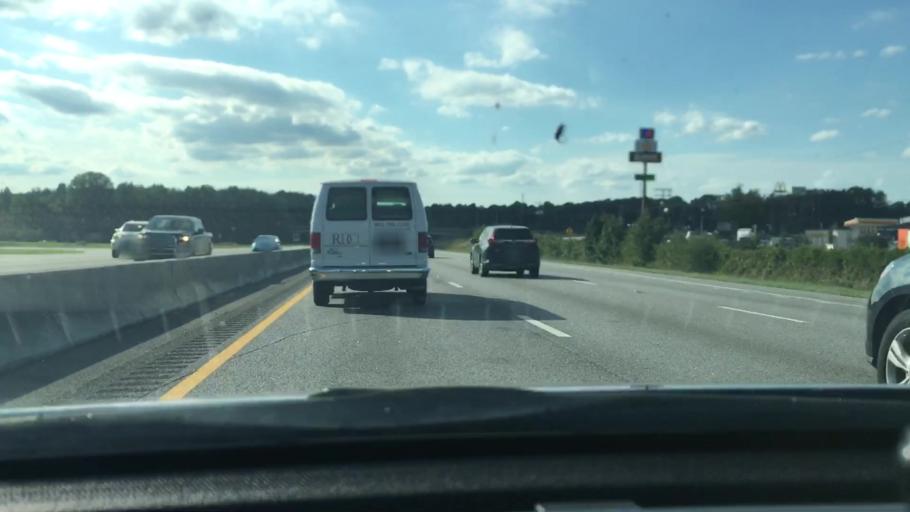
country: US
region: South Carolina
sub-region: Richland County
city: Dentsville
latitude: 34.0736
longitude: -80.9955
